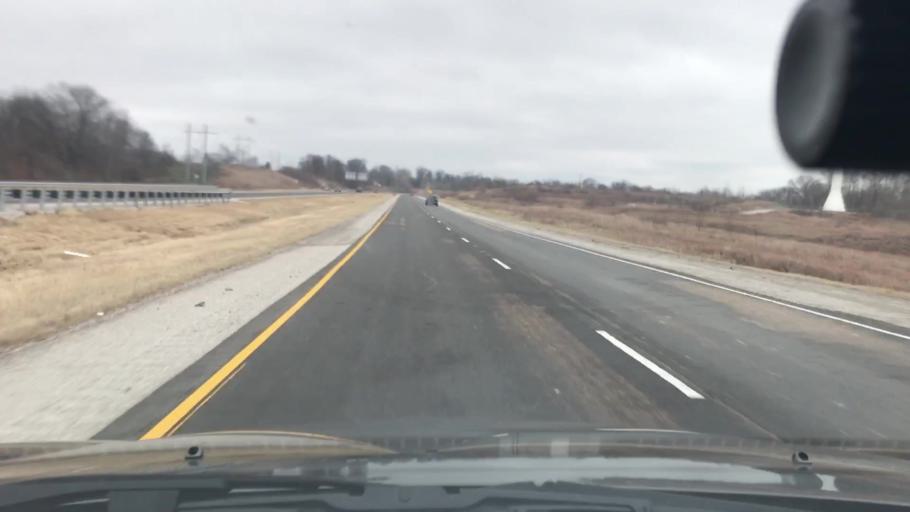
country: US
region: Illinois
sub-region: Madison County
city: Roxana
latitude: 38.8704
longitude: -90.0596
